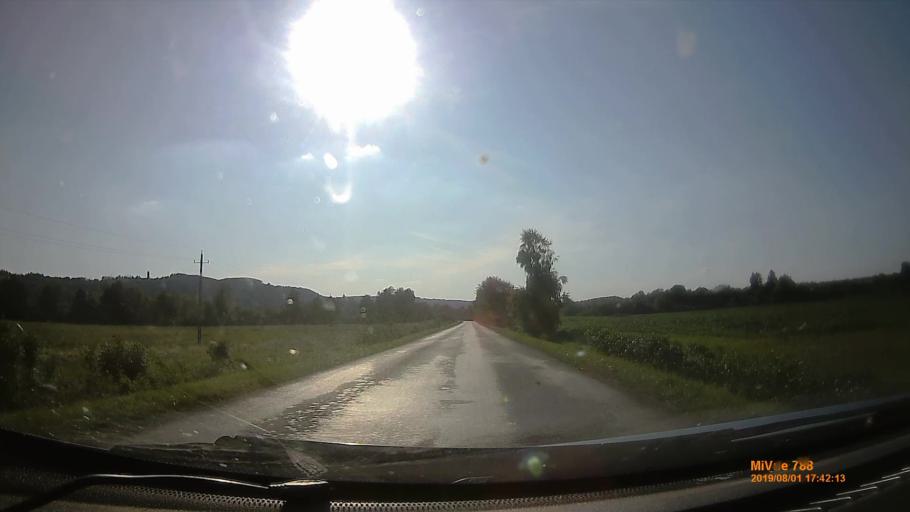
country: HU
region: Baranya
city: Sasd
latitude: 46.1899
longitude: 18.1654
